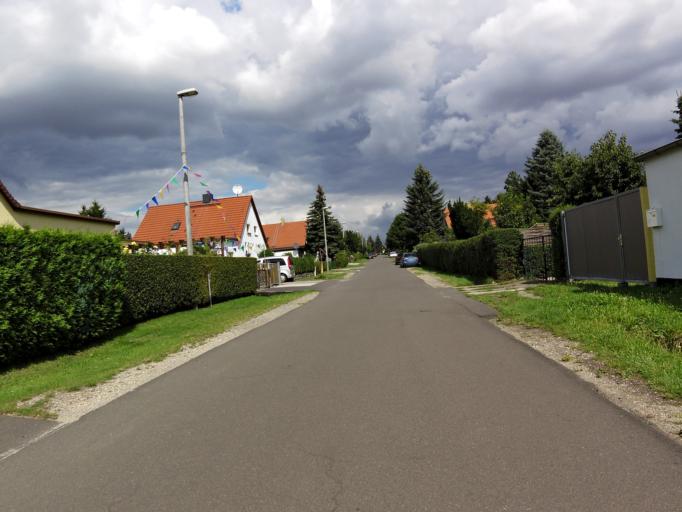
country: DE
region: Saxony
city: Rackwitz
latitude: 51.3824
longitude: 12.4112
